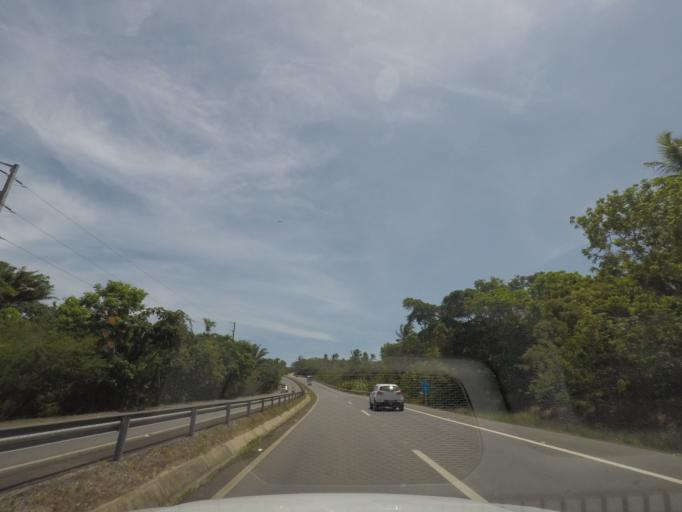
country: BR
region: Bahia
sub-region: Mata De Sao Joao
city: Mata de Sao Joao
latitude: -12.5766
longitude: -38.0407
